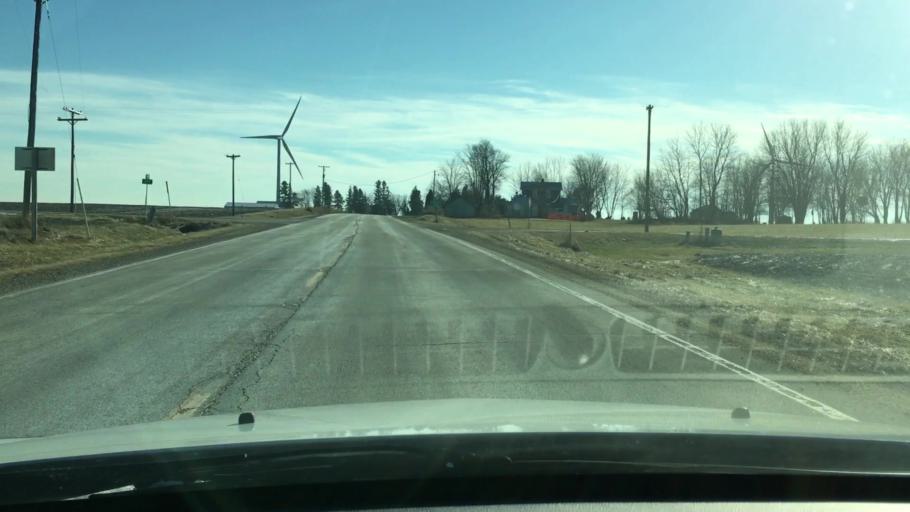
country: US
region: Illinois
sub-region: LaSalle County
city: Mendota
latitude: 41.6285
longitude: -89.1293
